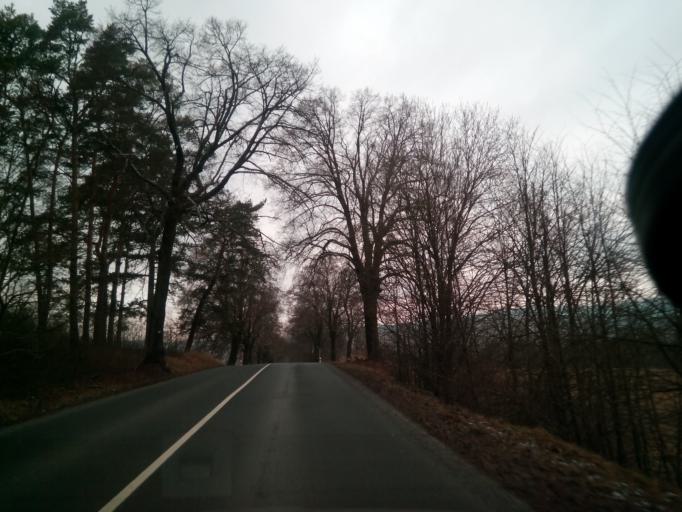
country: SK
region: Presovsky
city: Spisske Podhradie
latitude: 49.0075
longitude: 20.7286
